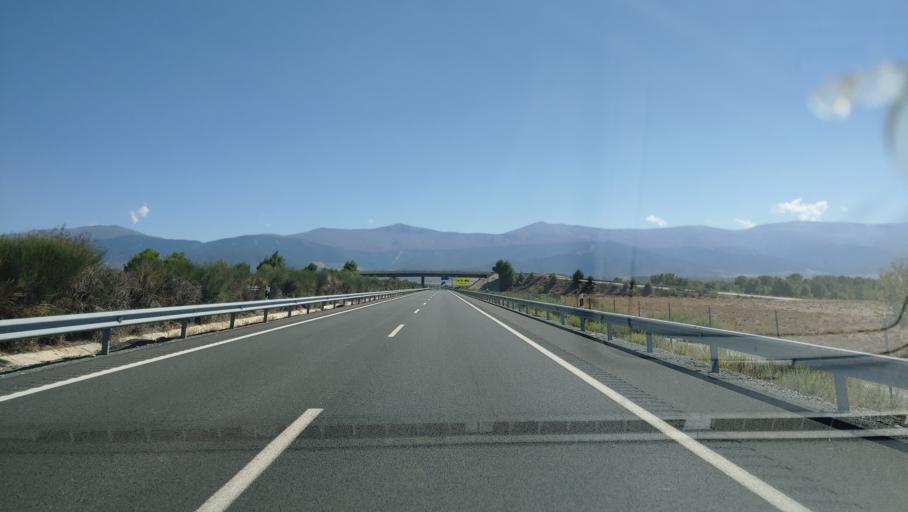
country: ES
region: Andalusia
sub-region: Provincia de Granada
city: Albunan
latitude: 37.2484
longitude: -3.0818
